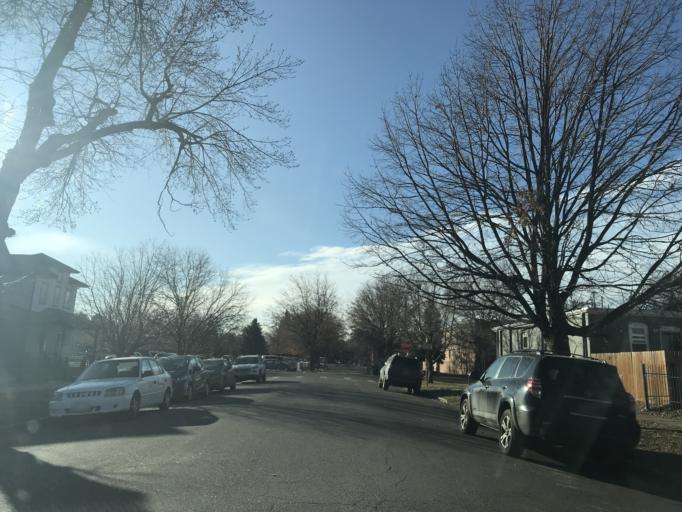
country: US
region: Colorado
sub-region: Denver County
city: Denver
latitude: 39.7639
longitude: -104.9709
